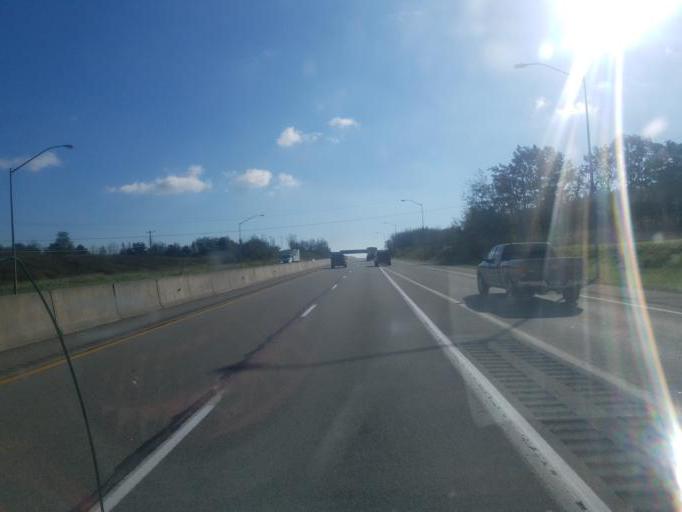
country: US
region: Pennsylvania
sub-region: Cambria County
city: Ebensburg
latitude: 40.4801
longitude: -78.7028
